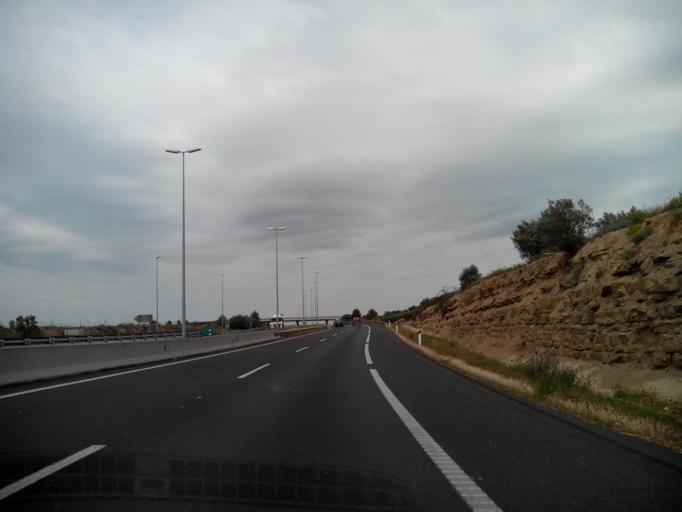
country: ES
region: Catalonia
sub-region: Provincia de Lleida
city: Tarrega
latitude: 41.6574
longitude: 1.1631
